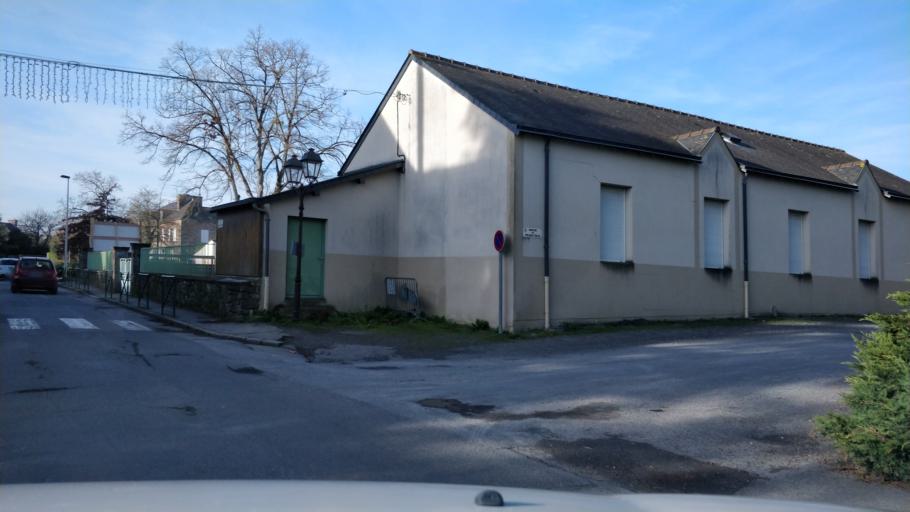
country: FR
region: Brittany
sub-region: Departement d'Ille-et-Vilaine
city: Plerguer
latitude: 48.5276
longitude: -1.8456
